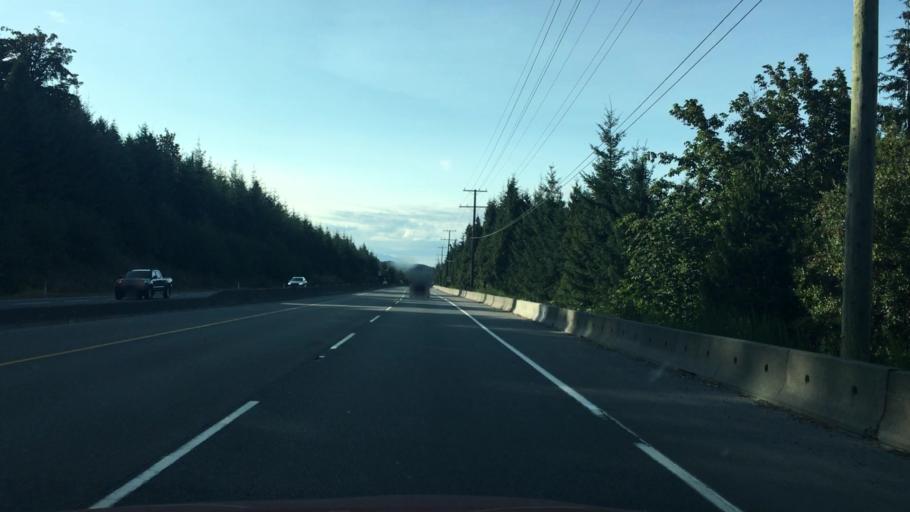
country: CA
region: British Columbia
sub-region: Cowichan Valley Regional District
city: Ladysmith
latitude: 48.9323
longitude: -123.7571
